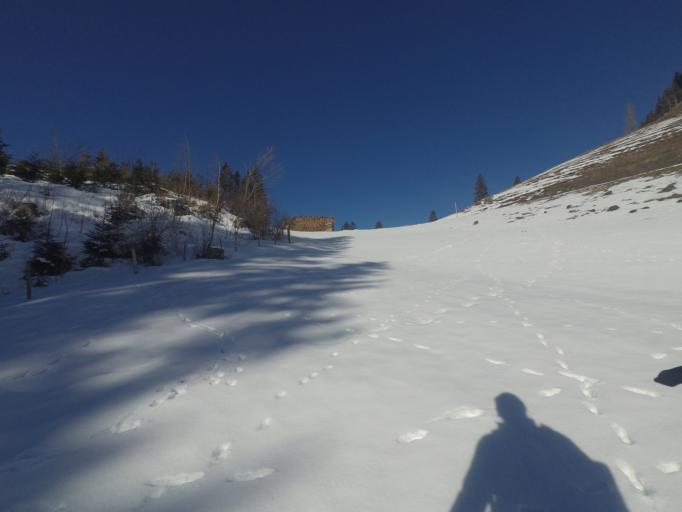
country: AT
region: Salzburg
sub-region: Politischer Bezirk Zell am See
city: Lend
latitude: 47.3212
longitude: 13.0379
